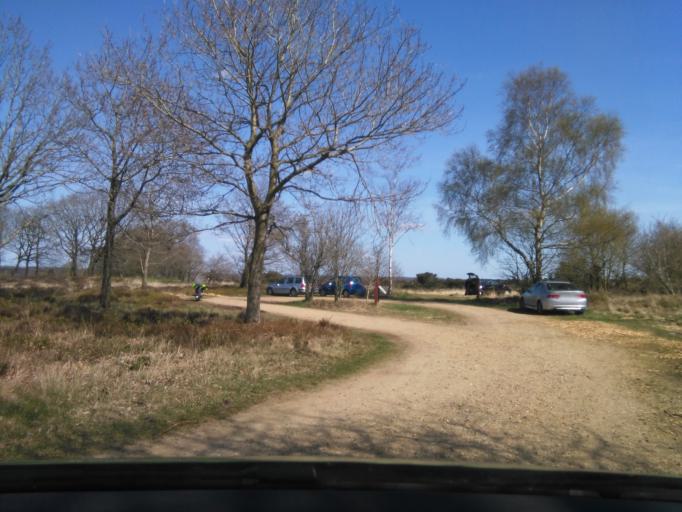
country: DK
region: Central Jutland
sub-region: Viborg Kommune
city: Viborg
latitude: 56.3827
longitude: 9.3047
